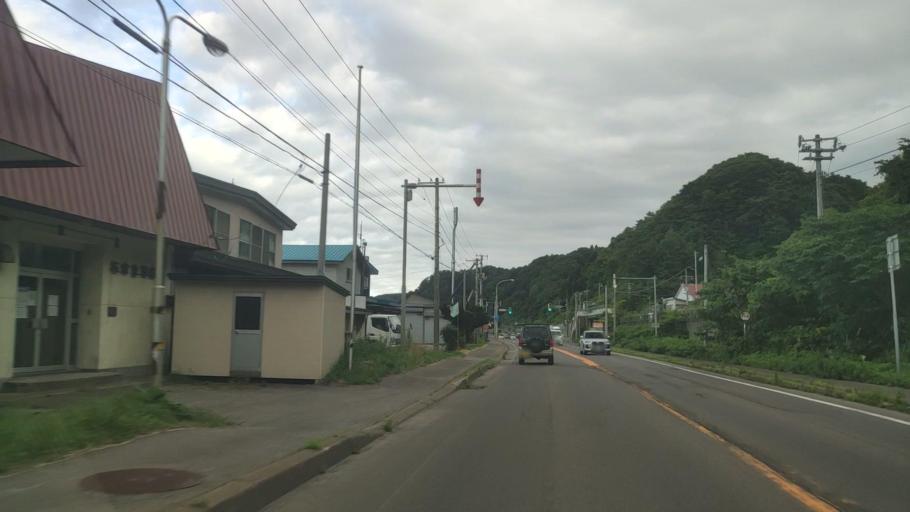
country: JP
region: Hokkaido
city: Nanae
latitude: 42.1607
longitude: 140.4713
